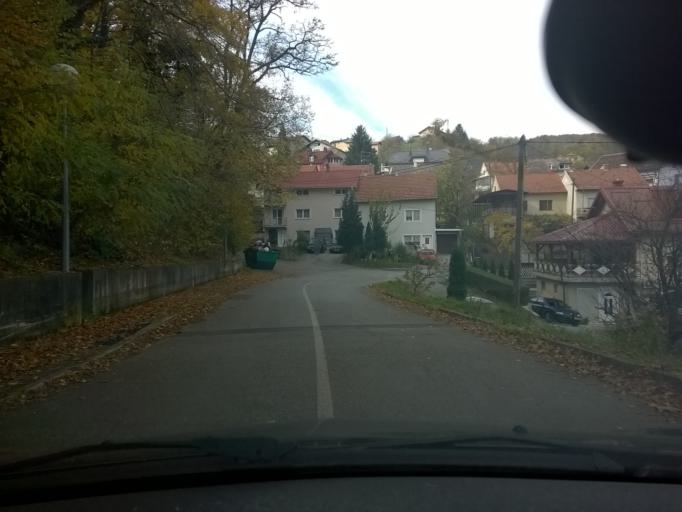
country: HR
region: Krapinsko-Zagorska
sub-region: Grad Krapina
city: Krapina
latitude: 46.1613
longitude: 15.8684
